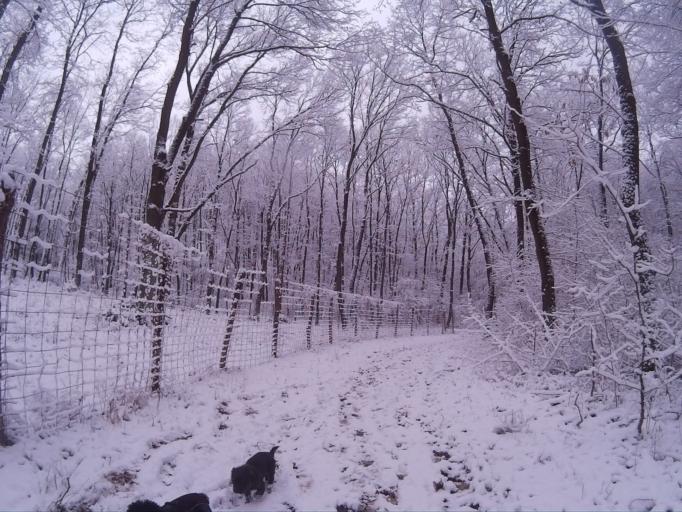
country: HU
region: Fejer
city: Szarliget
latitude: 47.5483
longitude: 18.5322
